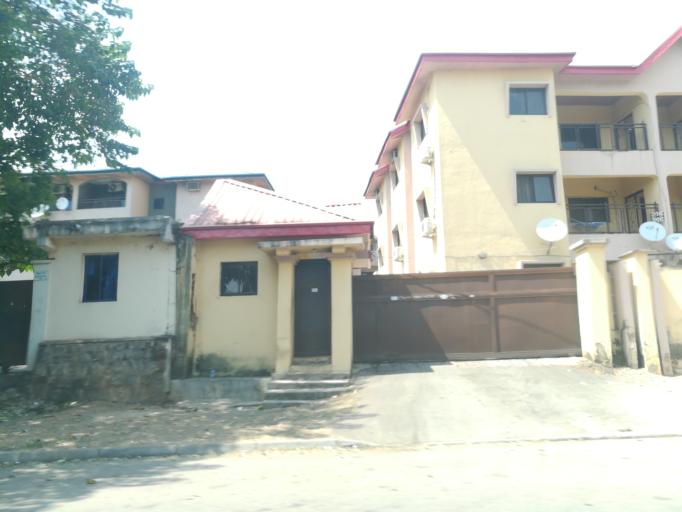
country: NG
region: Abuja Federal Capital Territory
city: Abuja
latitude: 9.0637
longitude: 7.4429
